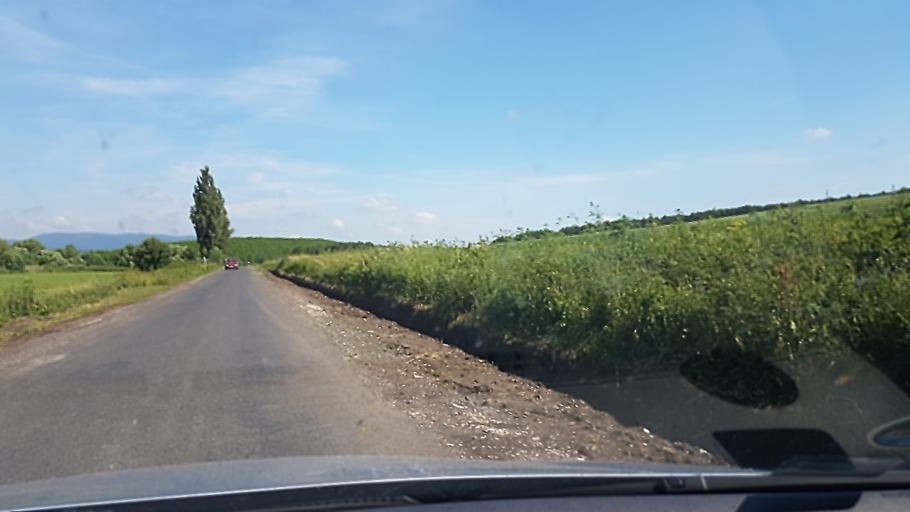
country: HU
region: Borsod-Abauj-Zemplen
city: Saly
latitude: 47.9370
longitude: 20.7103
